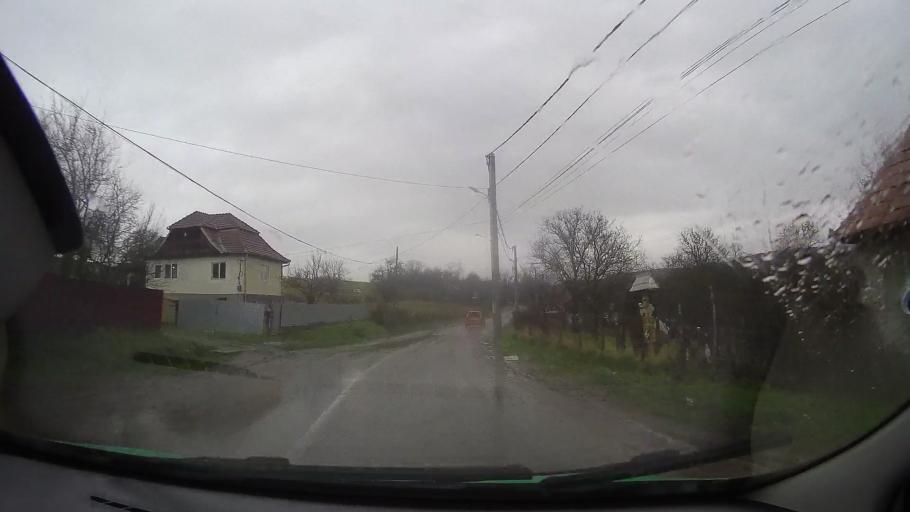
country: RO
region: Mures
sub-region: Comuna Vatava
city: Vatava
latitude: 46.9313
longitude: 24.7682
